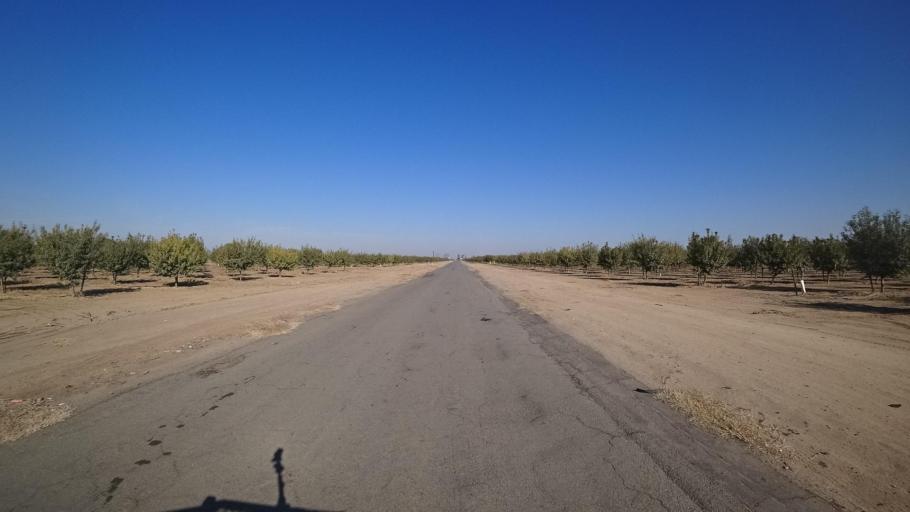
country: US
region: California
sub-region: Kern County
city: Delano
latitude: 35.7528
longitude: -119.2318
